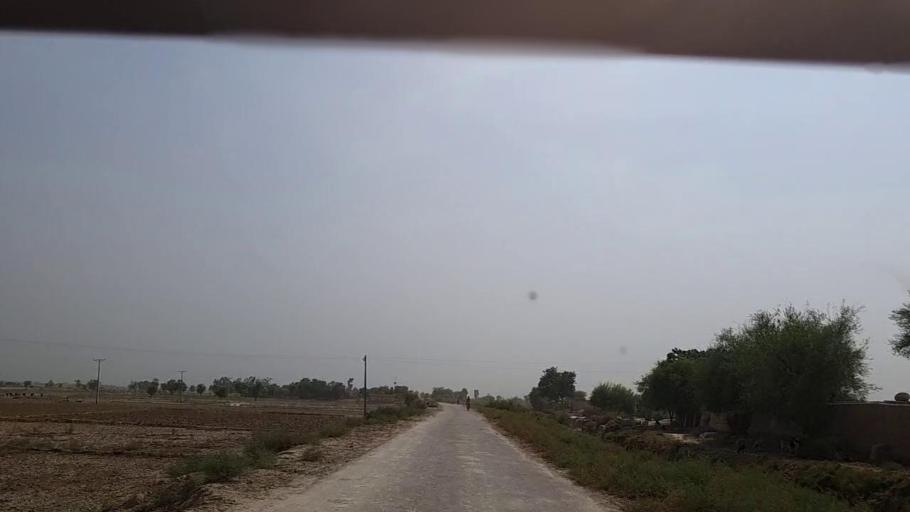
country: PK
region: Sindh
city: Khairpur Nathan Shah
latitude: 27.0368
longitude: 67.6843
